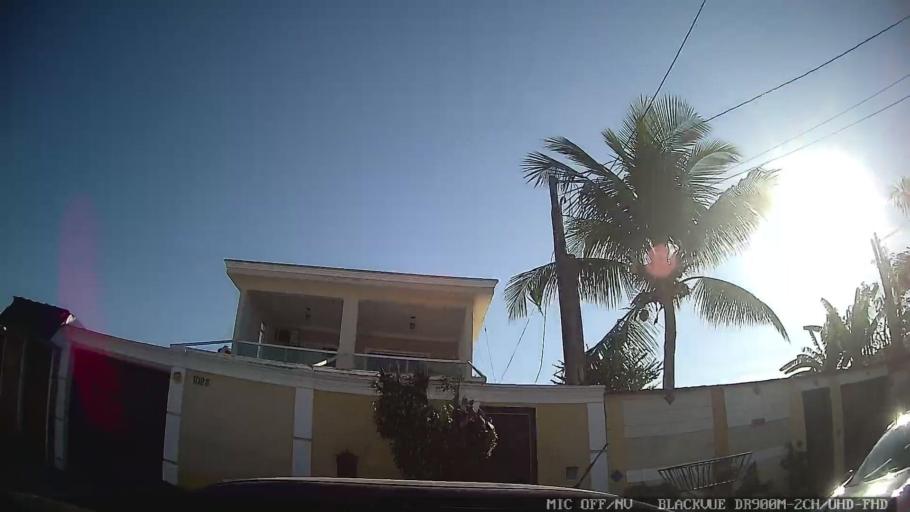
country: BR
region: Sao Paulo
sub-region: Guaruja
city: Guaruja
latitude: -23.9766
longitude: -46.2241
